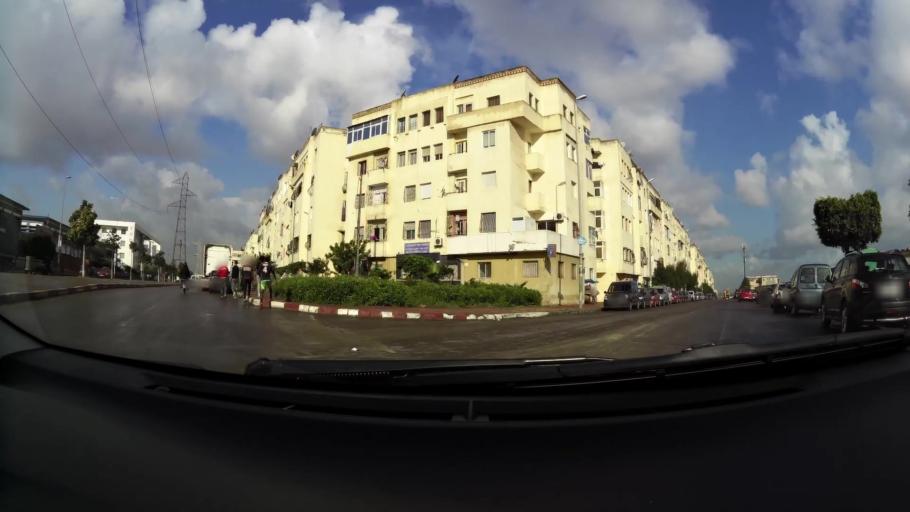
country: MA
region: Grand Casablanca
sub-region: Mediouna
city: Tit Mellil
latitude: 33.5944
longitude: -7.5310
